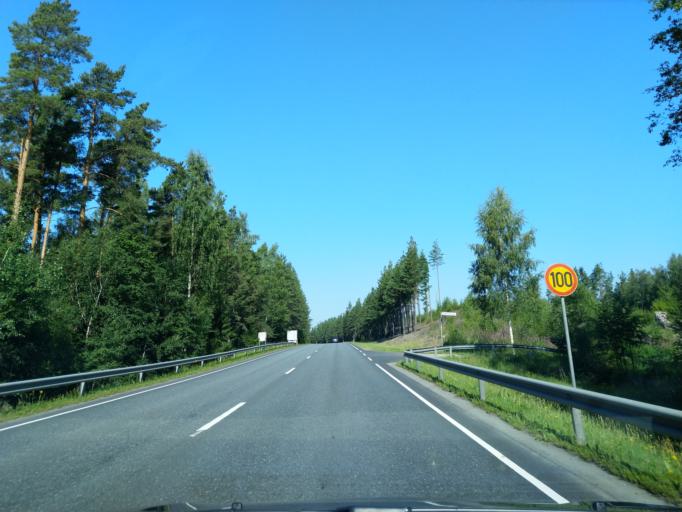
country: FI
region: Haeme
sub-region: Forssa
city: Humppila
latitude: 60.9709
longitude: 23.2741
